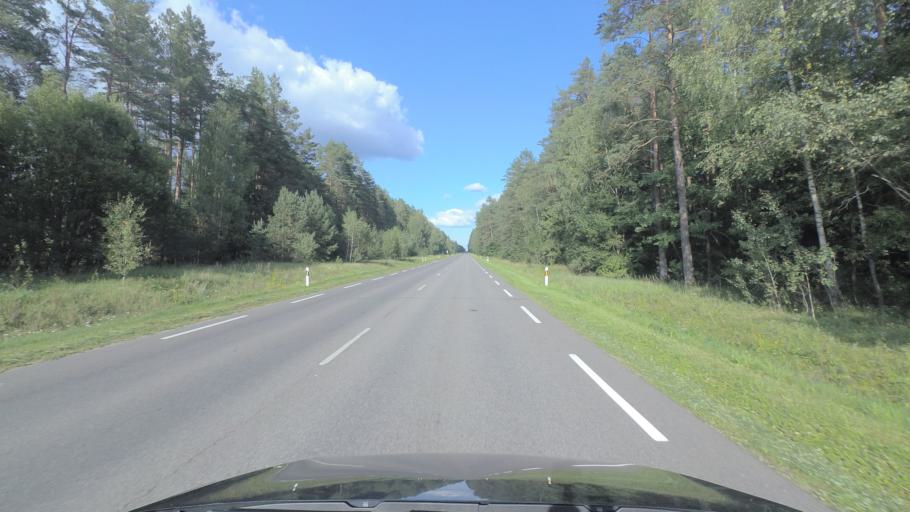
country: LT
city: Pabrade
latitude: 54.9682
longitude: 25.7203
